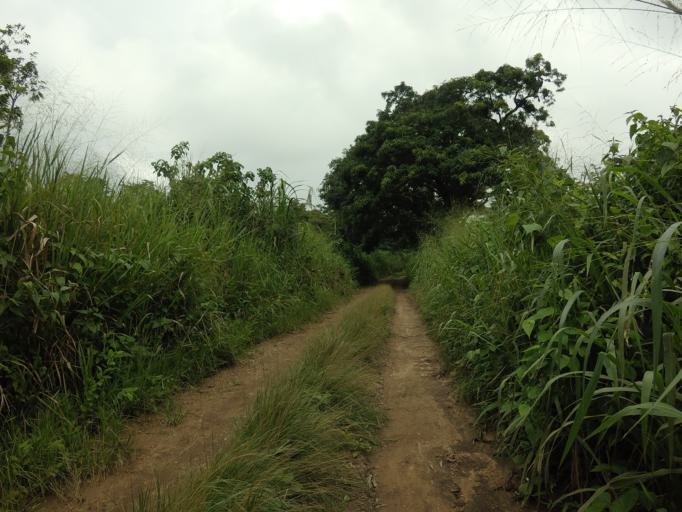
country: TG
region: Plateaux
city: Kpalime
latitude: 6.8430
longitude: 0.4458
